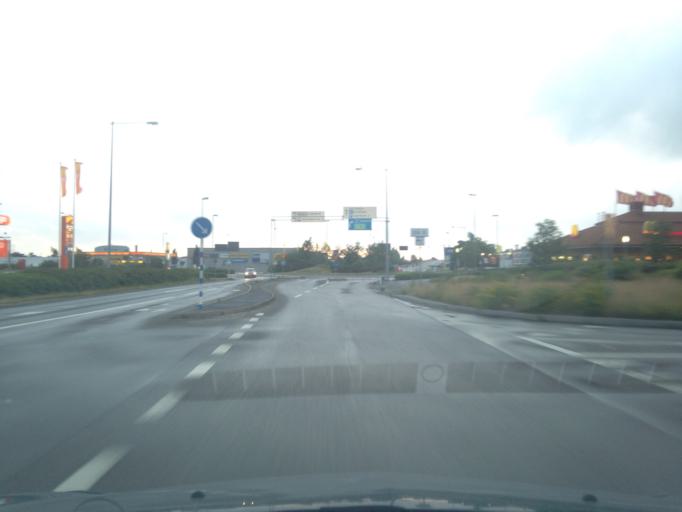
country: SE
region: Halland
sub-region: Varbergs Kommun
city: Varberg
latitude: 57.1234
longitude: 12.2639
